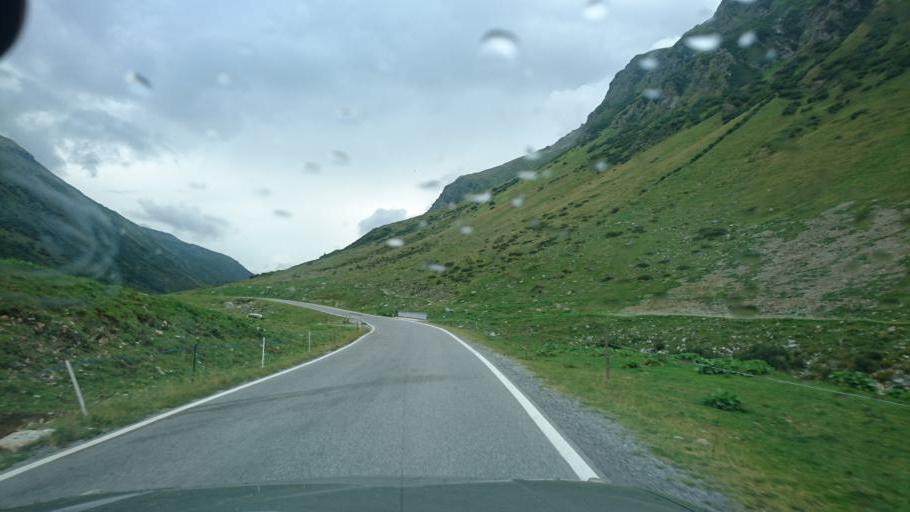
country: AT
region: Tyrol
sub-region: Politischer Bezirk Landeck
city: Galtur
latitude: 46.9355
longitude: 10.1331
